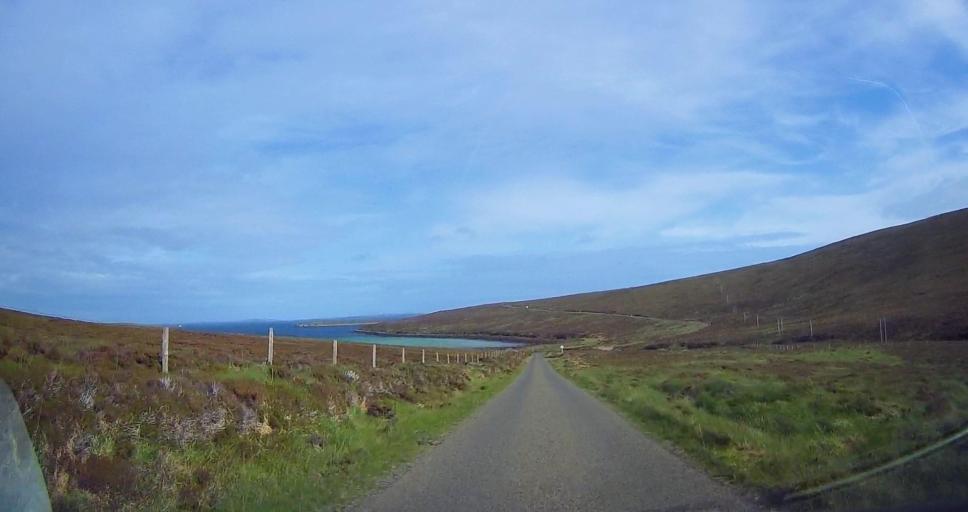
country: GB
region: Scotland
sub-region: Orkney Islands
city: Stromness
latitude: 58.8721
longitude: -3.2369
